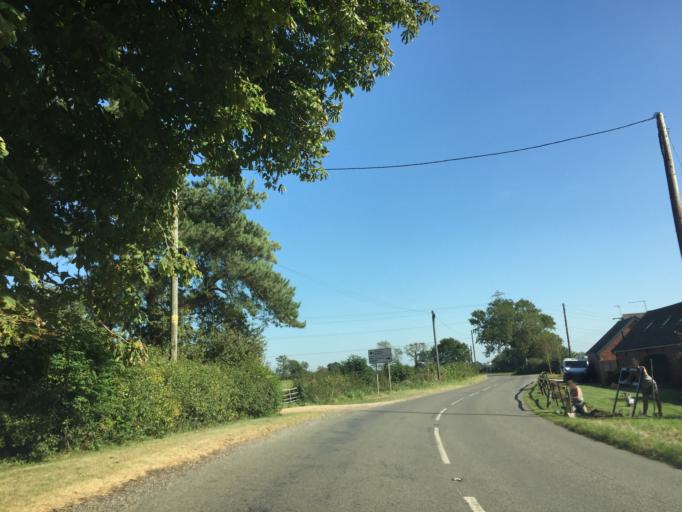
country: GB
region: England
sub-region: Leicestershire
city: Houghton on the Hill
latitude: 52.6411
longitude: -0.9160
